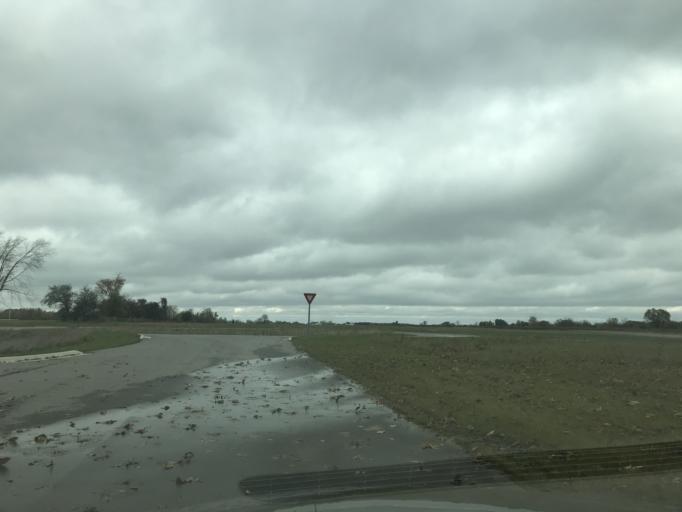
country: US
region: Michigan
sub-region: Eaton County
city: Grand Ledge
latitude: 42.7132
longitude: -84.6934
